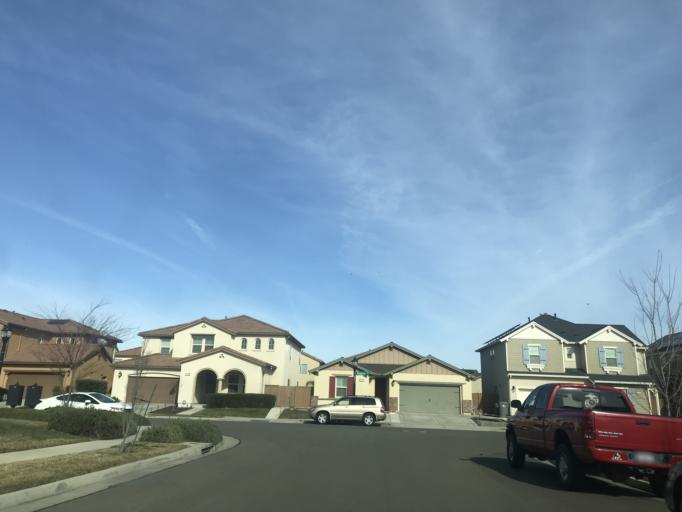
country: US
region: California
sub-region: Yolo County
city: Woodland
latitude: 38.6571
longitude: -121.7590
